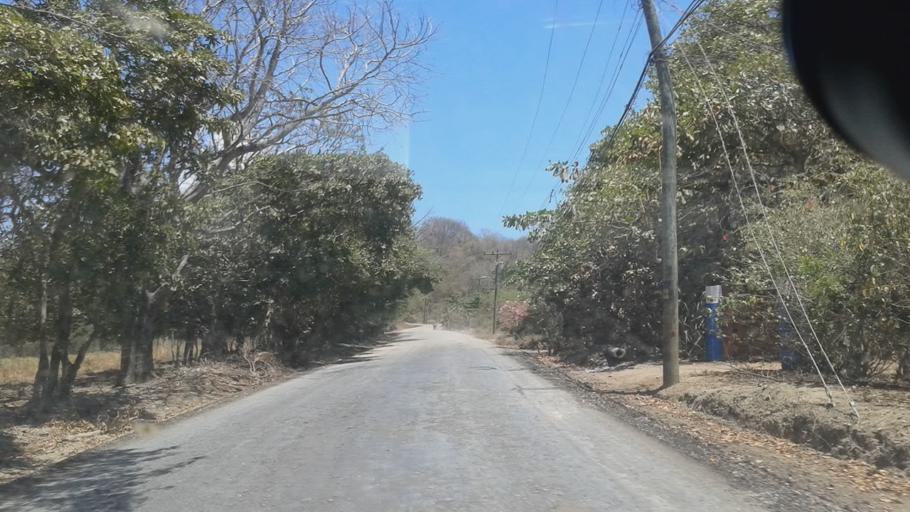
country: CR
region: Guanacaste
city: Samara
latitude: 10.0054
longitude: -85.7107
